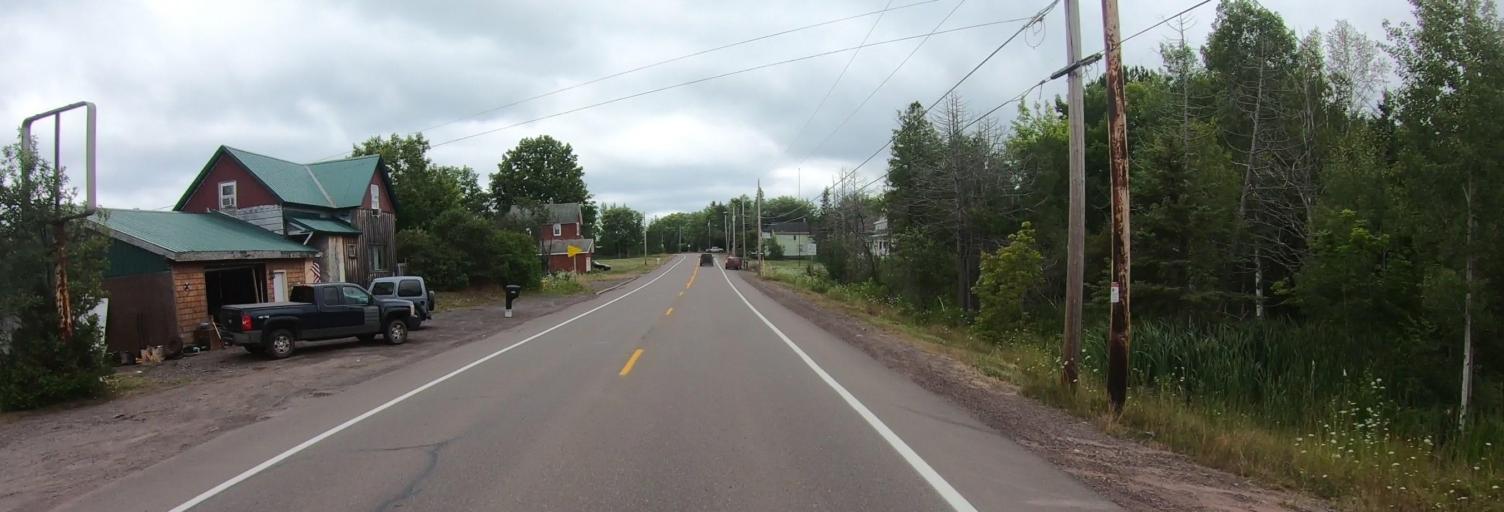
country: US
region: Michigan
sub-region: Houghton County
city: Laurium
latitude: 47.2675
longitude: -88.4226
